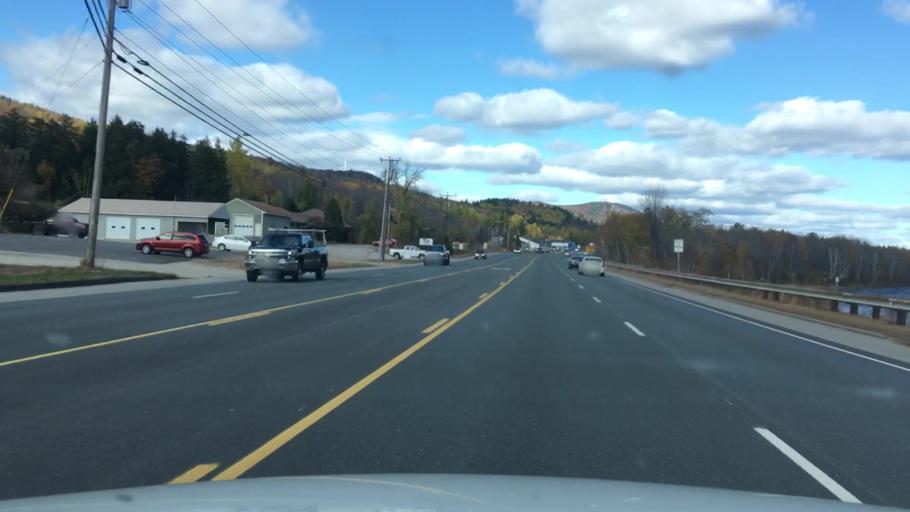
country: US
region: New Hampshire
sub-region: Coos County
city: Gorham
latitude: 44.4179
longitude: -71.1940
